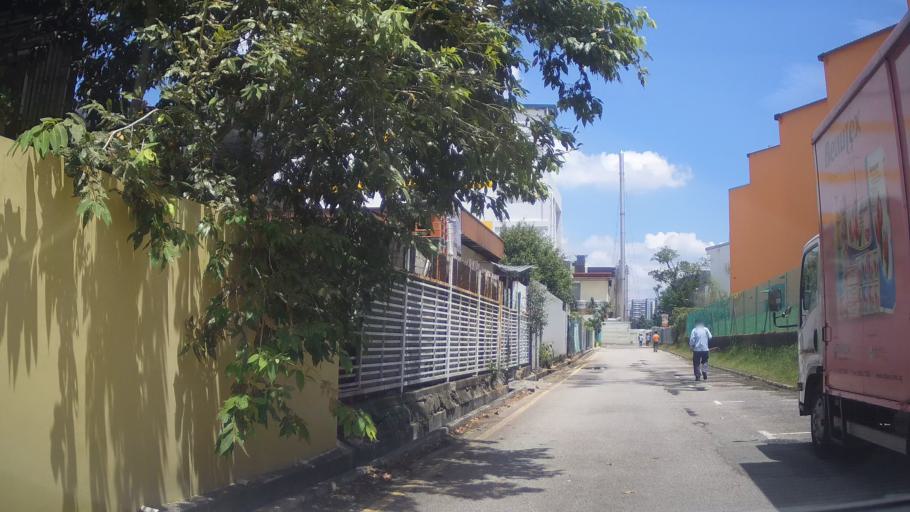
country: MY
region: Johor
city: Johor Bahru
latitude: 1.3335
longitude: 103.7110
